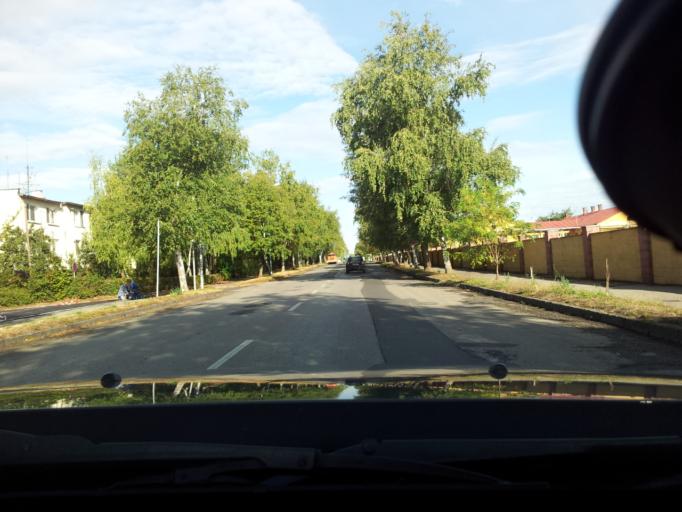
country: SK
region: Kosicky
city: Michalovce
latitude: 48.7634
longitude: 21.9075
